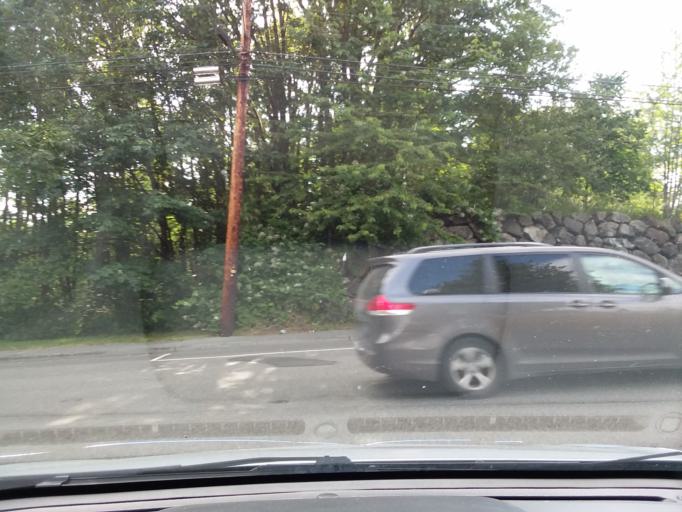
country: US
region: Washington
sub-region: Snohomish County
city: Mountlake Terrace
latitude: 47.7909
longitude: -122.2976
